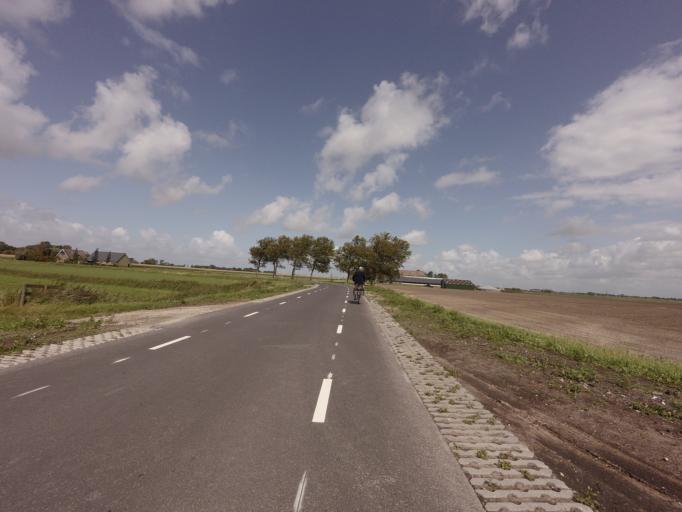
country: NL
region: Friesland
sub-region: Gemeente Harlingen
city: Harlingen
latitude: 53.1527
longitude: 5.4779
